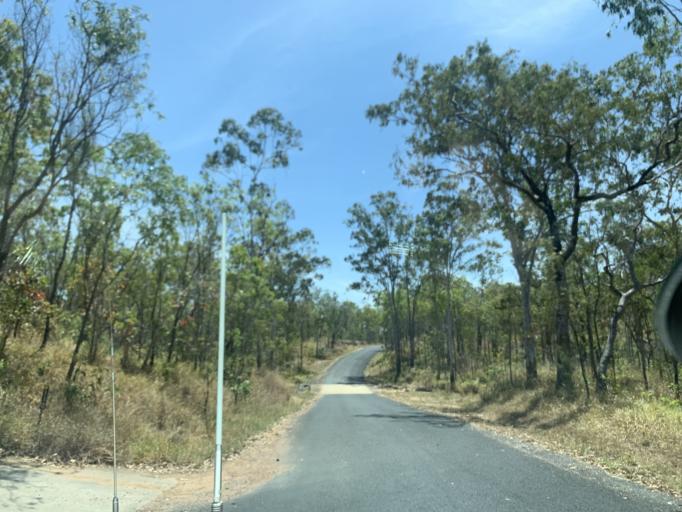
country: AU
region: Queensland
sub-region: Tablelands
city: Kuranda
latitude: -16.9115
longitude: 145.5750
